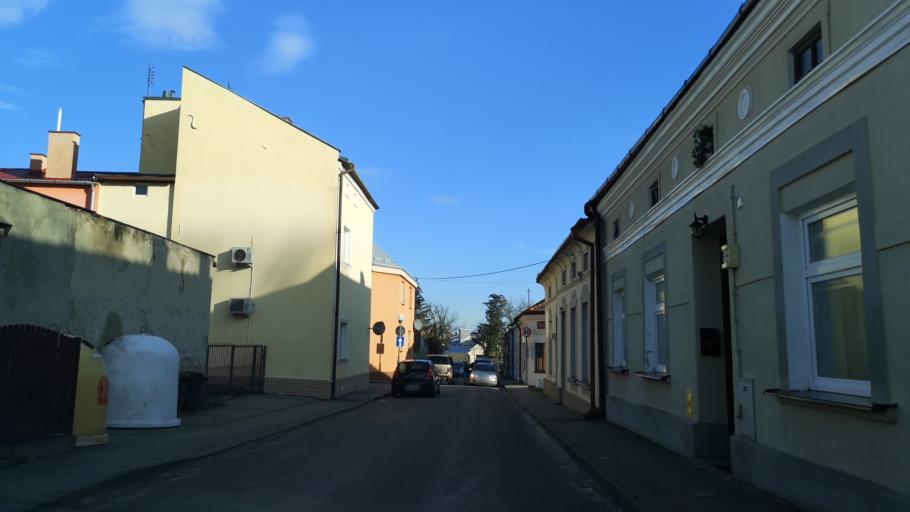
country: PL
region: Subcarpathian Voivodeship
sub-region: Powiat lezajski
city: Lezajsk
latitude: 50.2524
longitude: 22.4234
